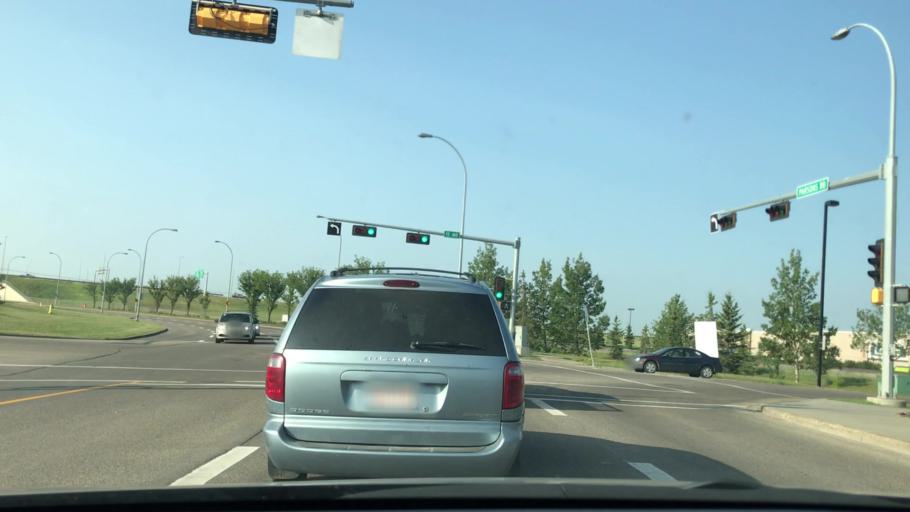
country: CA
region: Alberta
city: Edmonton
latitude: 53.4414
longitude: -113.4839
